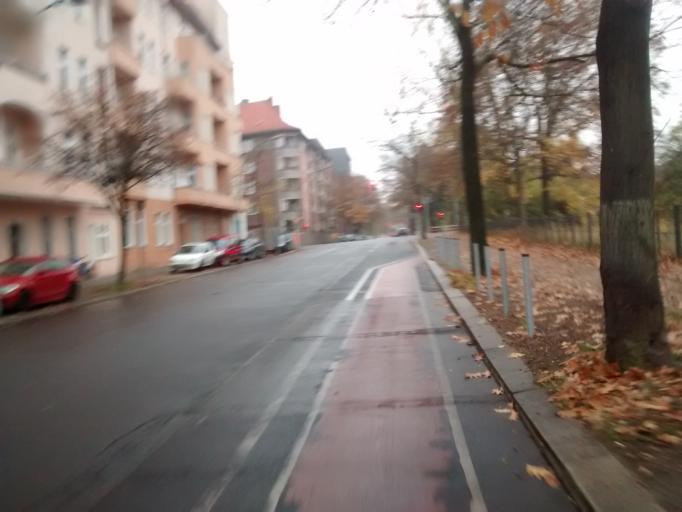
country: DE
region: Berlin
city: Charlottenburg-Nord
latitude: 52.5265
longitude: 13.3157
